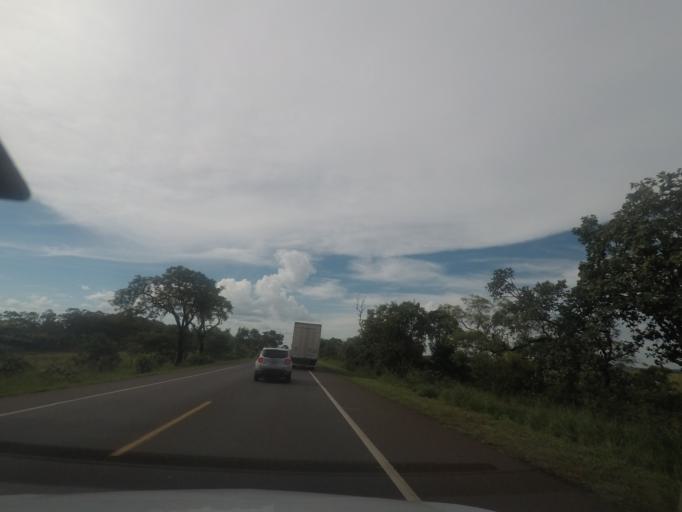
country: BR
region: Minas Gerais
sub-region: Prata
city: Prata
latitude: -19.2341
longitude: -48.9308
